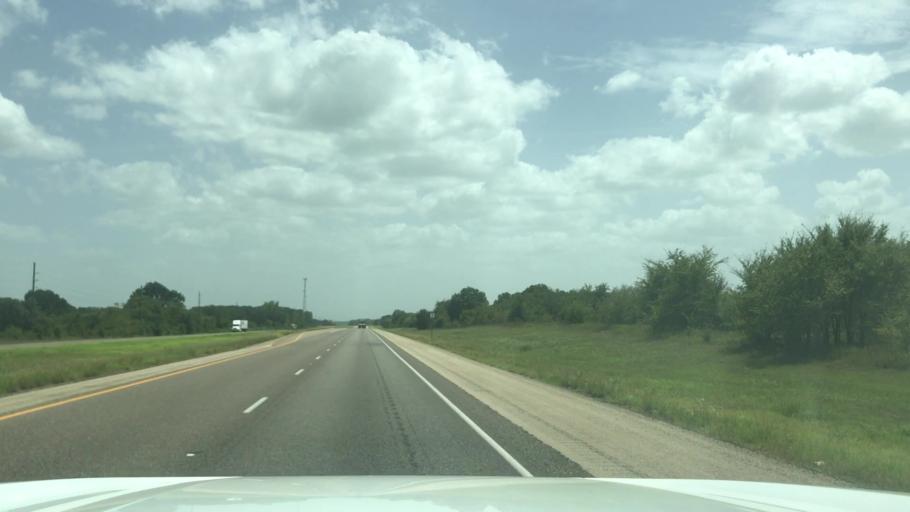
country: US
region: Texas
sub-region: Robertson County
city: Calvert
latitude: 31.0425
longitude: -96.7105
